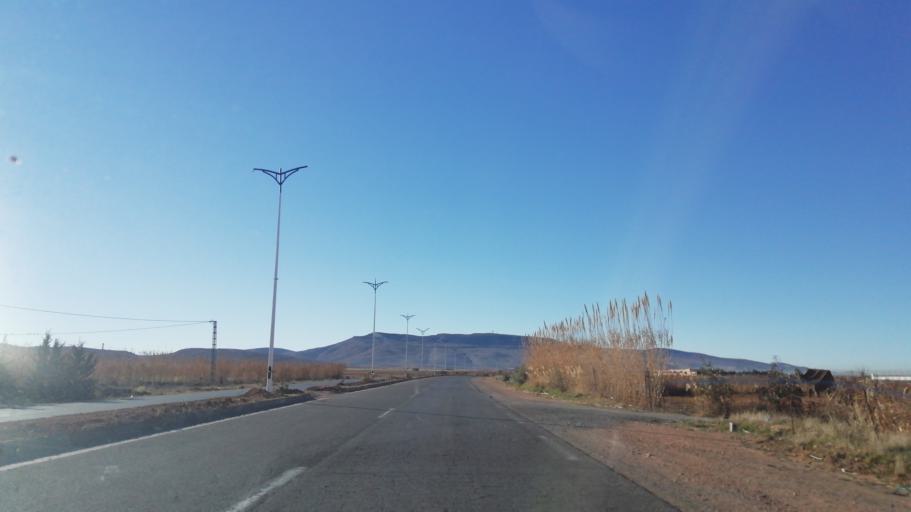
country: DZ
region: El Bayadh
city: El Bayadh
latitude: 33.6983
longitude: 1.0814
